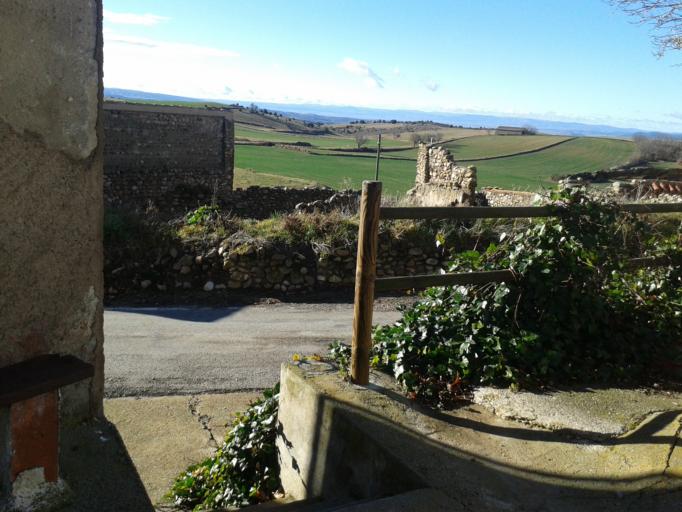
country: ES
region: Aragon
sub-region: Provincia de Teruel
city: Bea
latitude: 40.9902
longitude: -1.1644
